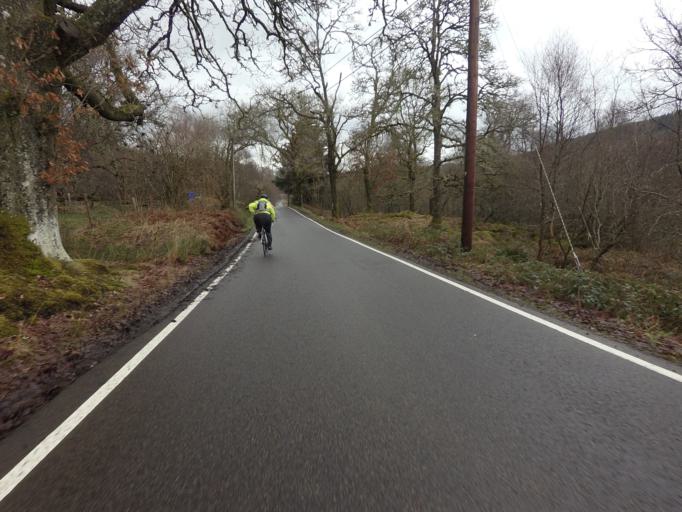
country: GB
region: Scotland
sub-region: West Dunbartonshire
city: Balloch
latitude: 56.1965
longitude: -4.5208
